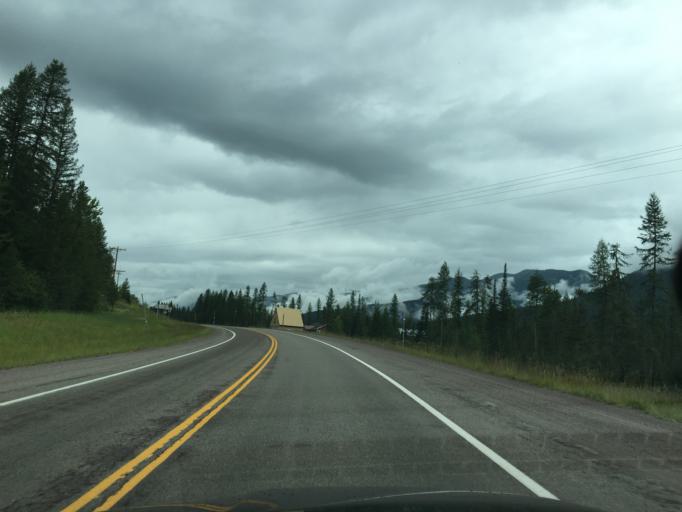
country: US
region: Montana
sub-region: Flathead County
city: Bigfork
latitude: 48.2835
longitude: -113.6065
